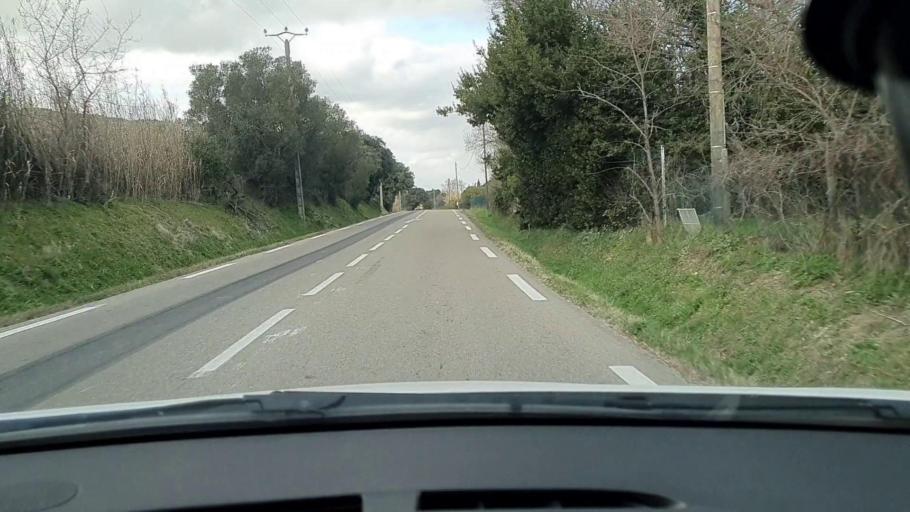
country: FR
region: Languedoc-Roussillon
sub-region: Departement du Gard
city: Remoulins
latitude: 43.9270
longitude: 4.5613
